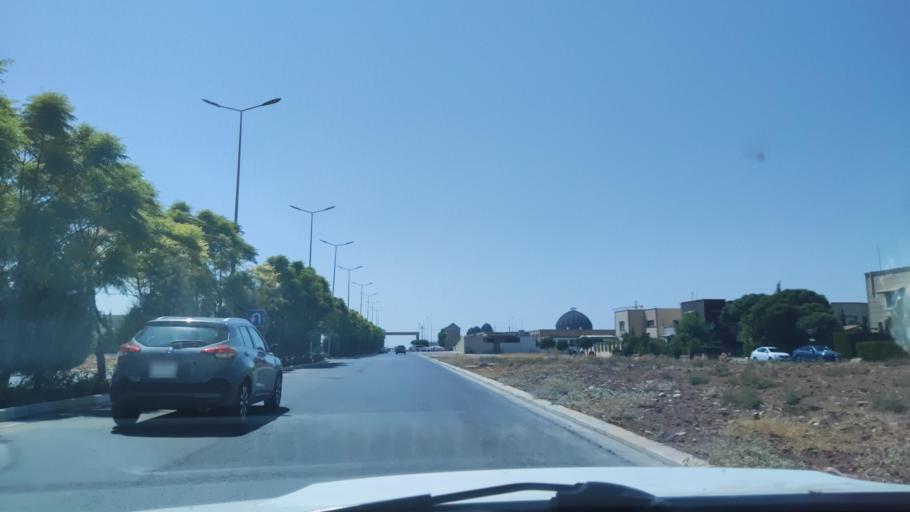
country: IQ
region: Arbil
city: Erbil
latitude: 36.2883
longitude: 44.0501
